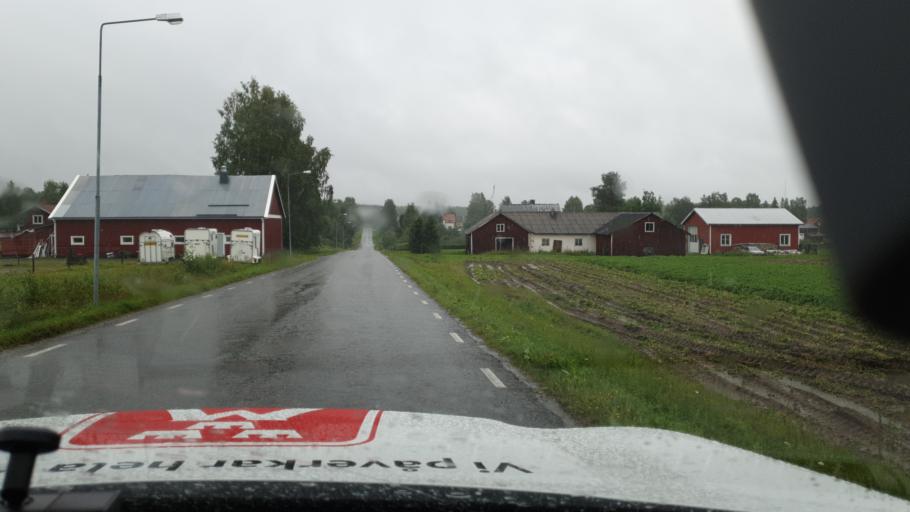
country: SE
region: Vaesterbotten
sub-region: Skelleftea Kommun
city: Viken
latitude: 64.8715
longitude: 20.8036
